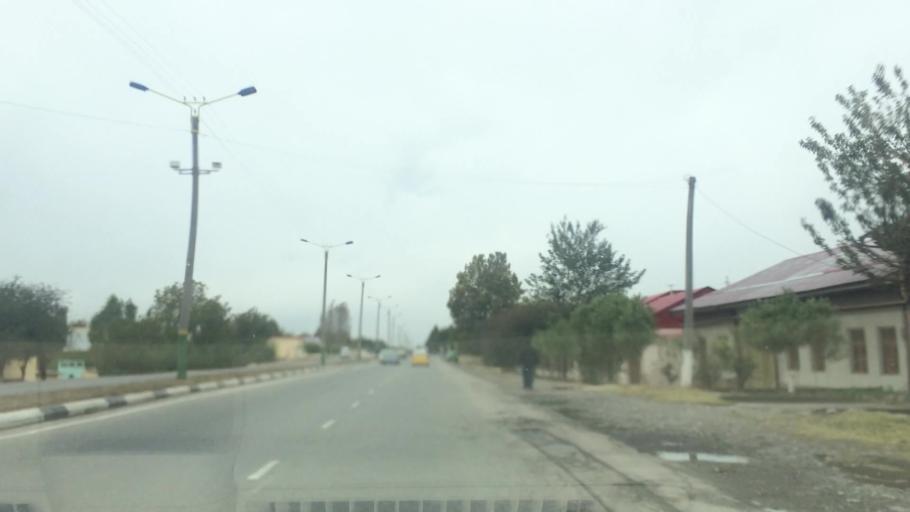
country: UZ
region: Samarqand
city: Bulung'ur
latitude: 39.7670
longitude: 67.2605
